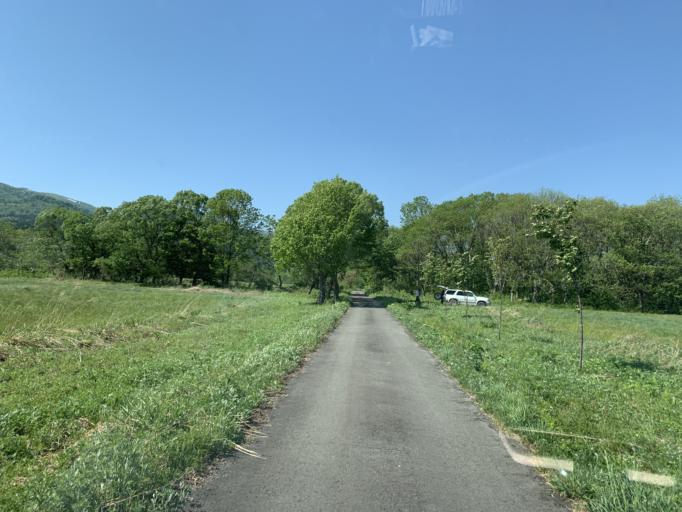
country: JP
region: Iwate
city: Shizukuishi
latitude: 39.5506
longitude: 140.8211
